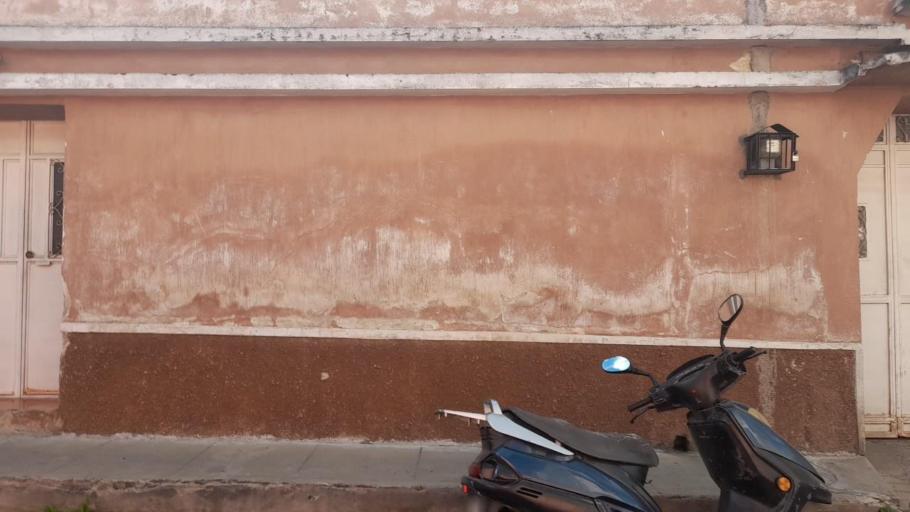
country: GT
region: Quetzaltenango
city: Quetzaltenango
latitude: 14.8281
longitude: -91.5156
